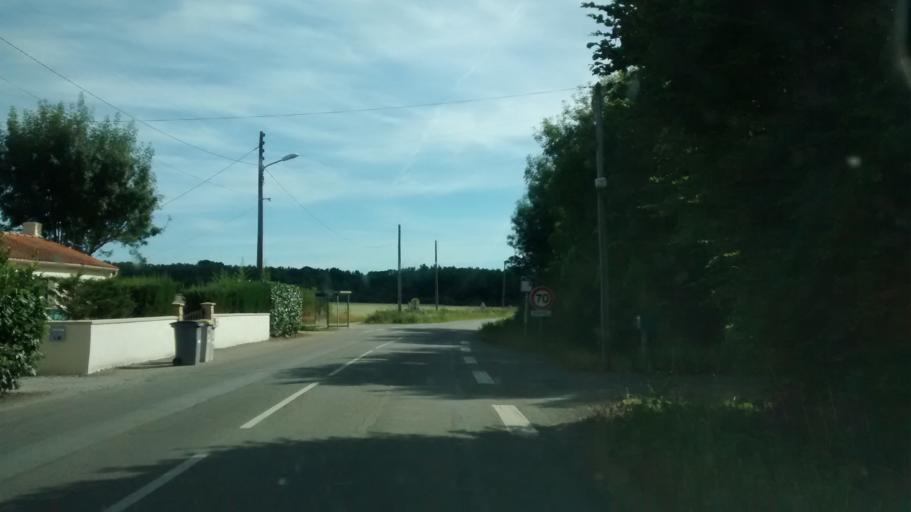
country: FR
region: Pays de la Loire
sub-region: Departement de la Loire-Atlantique
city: Pont-Saint-Martin
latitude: 47.1367
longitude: -1.6104
